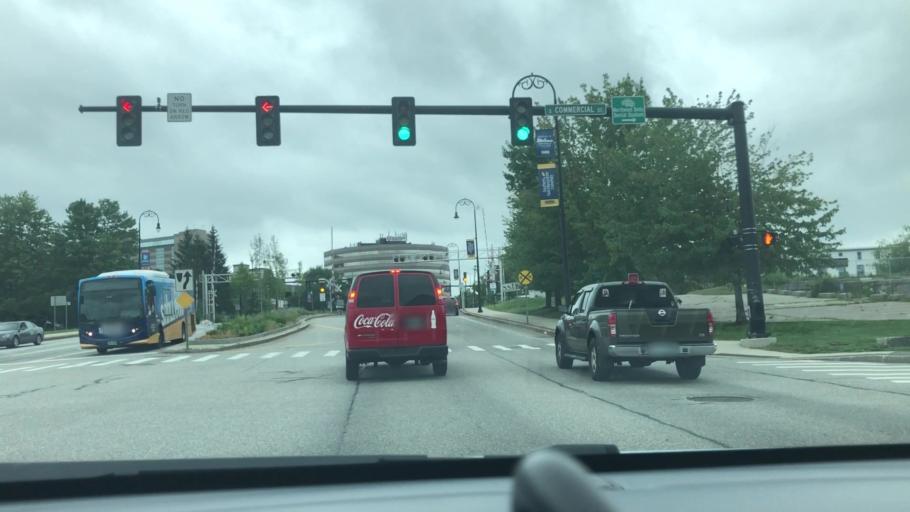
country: US
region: New Hampshire
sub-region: Hillsborough County
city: Manchester
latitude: 42.9860
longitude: -71.4677
